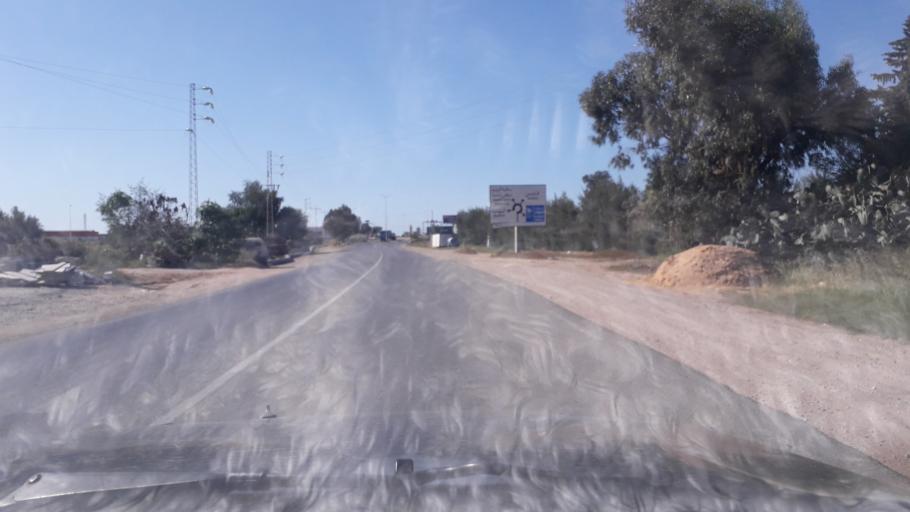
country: TN
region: Safaqis
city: Al Qarmadah
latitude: 34.8589
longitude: 10.7594
